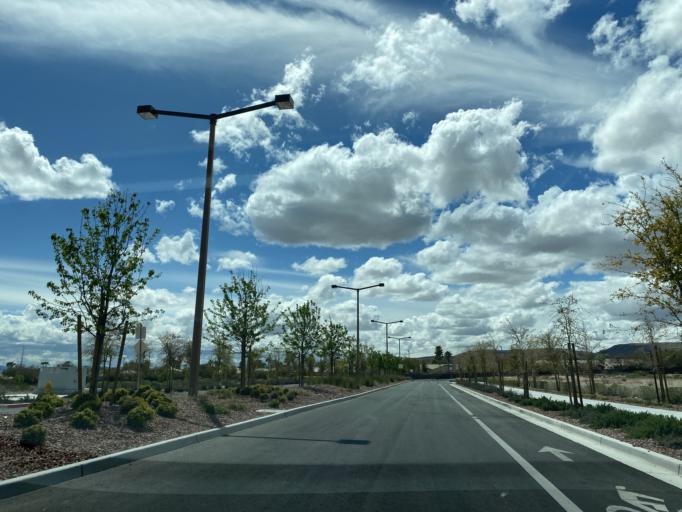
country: US
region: Nevada
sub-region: Clark County
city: Summerlin South
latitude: 36.1169
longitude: -115.3195
